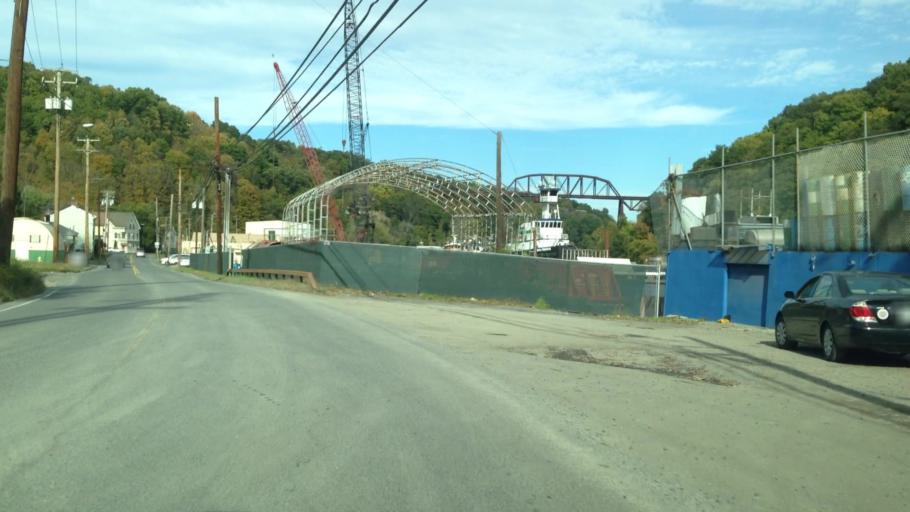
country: US
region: New York
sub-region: Ulster County
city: Kingston
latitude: 41.9066
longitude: -74.0053
